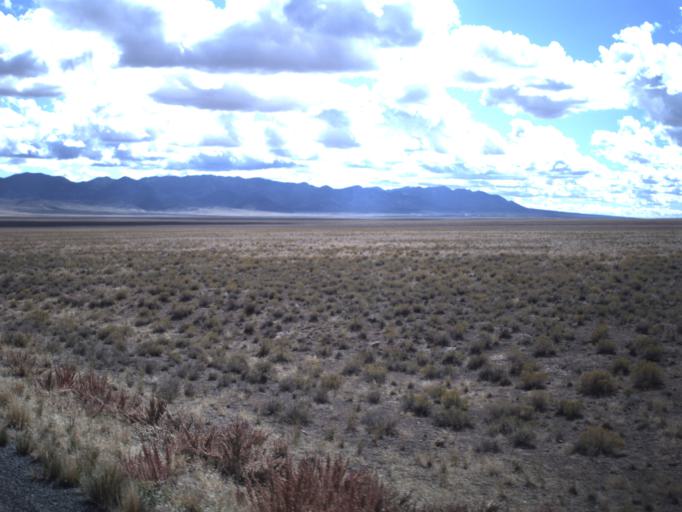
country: US
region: Utah
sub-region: Beaver County
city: Milford
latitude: 38.5591
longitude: -113.7545
